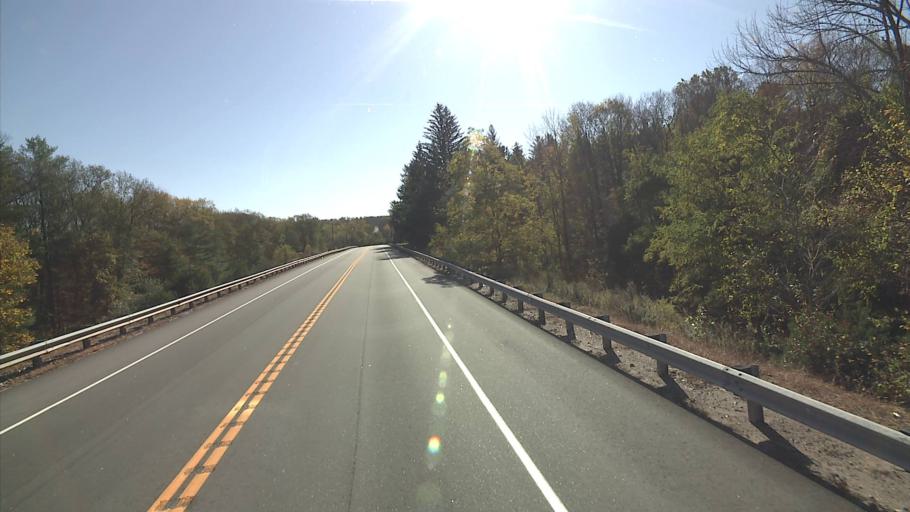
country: US
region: Connecticut
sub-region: Tolland County
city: Coventry Lake
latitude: 41.7299
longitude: -72.3536
